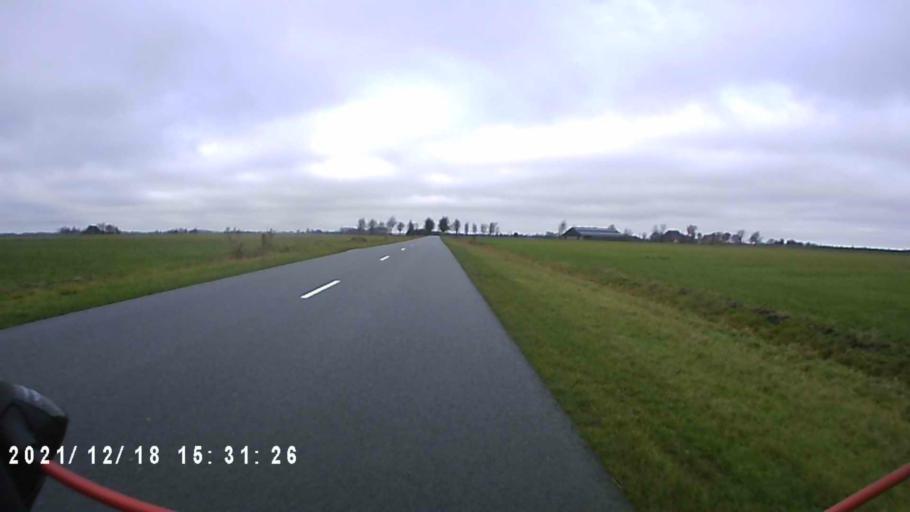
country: NL
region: Friesland
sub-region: Gemeente Dongeradeel
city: Anjum
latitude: 53.3393
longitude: 6.1369
